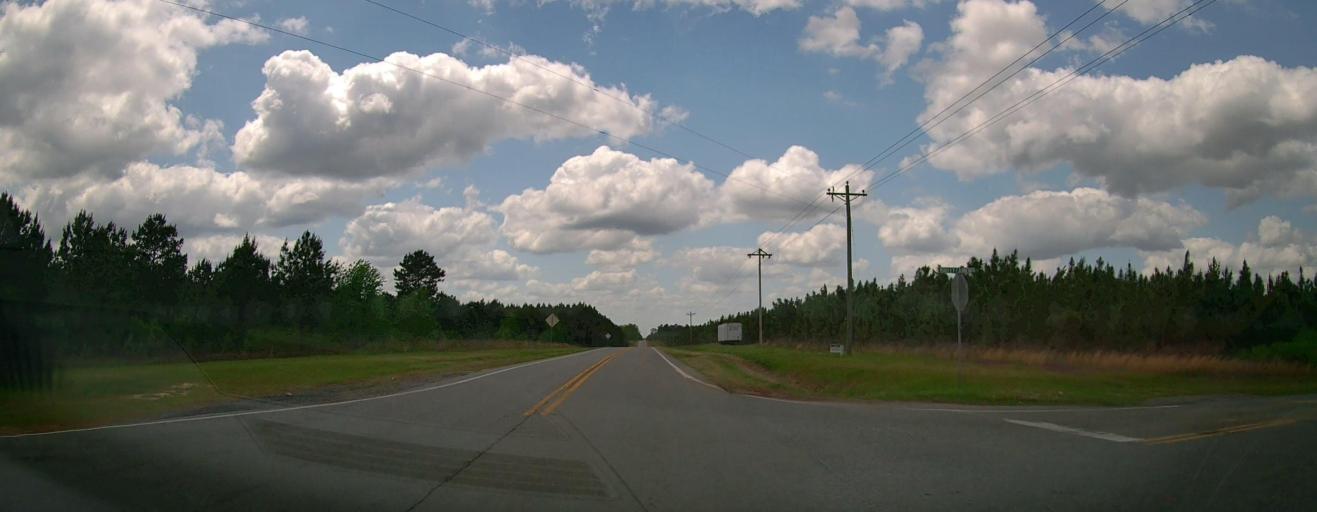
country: US
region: Georgia
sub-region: Laurens County
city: Dublin
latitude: 32.5848
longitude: -83.0137
